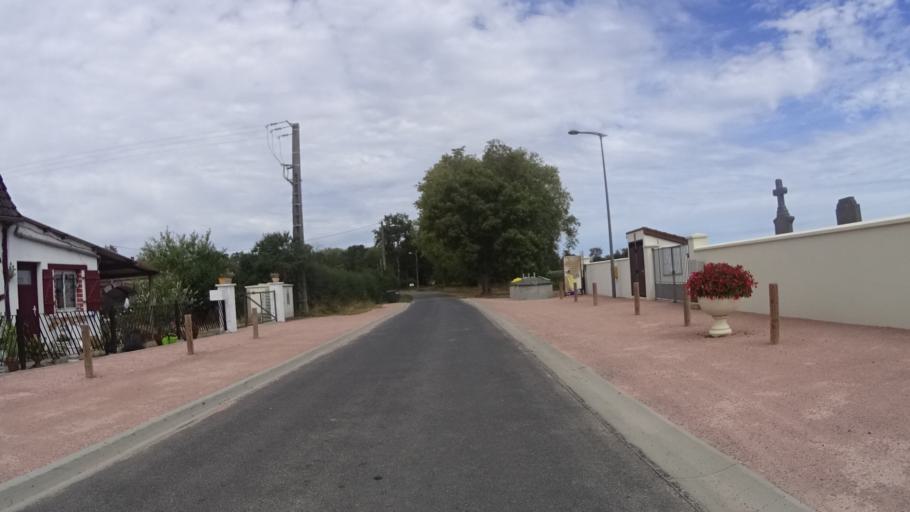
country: FR
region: Auvergne
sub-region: Departement de l'Allier
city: Beaulon
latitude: 46.6680
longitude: 3.6545
